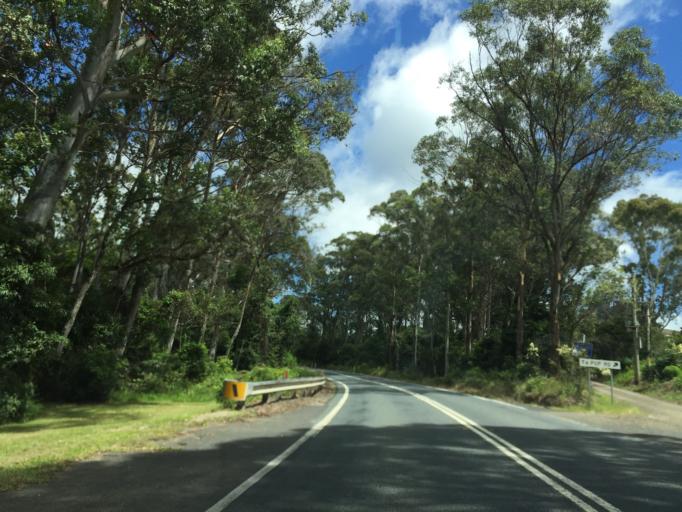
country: AU
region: New South Wales
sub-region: Hawkesbury
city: Richmond
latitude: -33.5025
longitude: 150.5403
